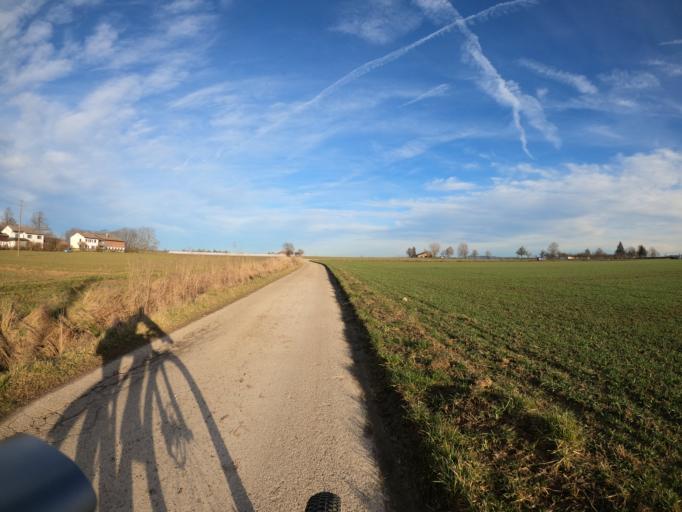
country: DE
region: Baden-Wuerttemberg
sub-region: Regierungsbezirk Stuttgart
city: Denkendorf
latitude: 48.6908
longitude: 9.3393
